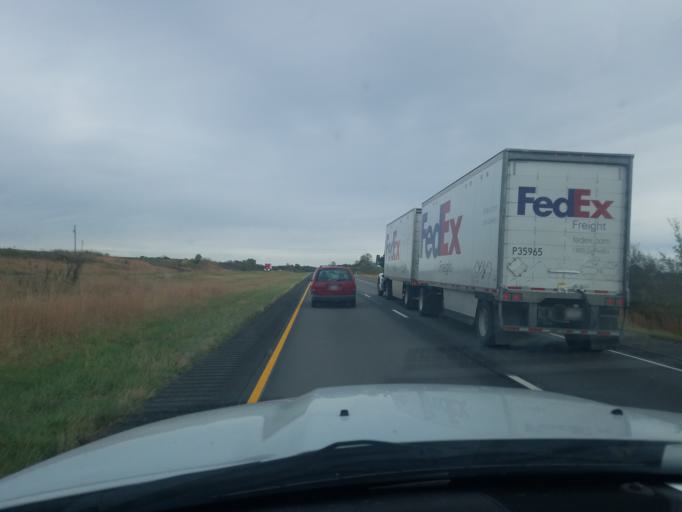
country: US
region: Indiana
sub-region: Dubois County
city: Ferdinand
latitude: 38.2024
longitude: -86.8282
